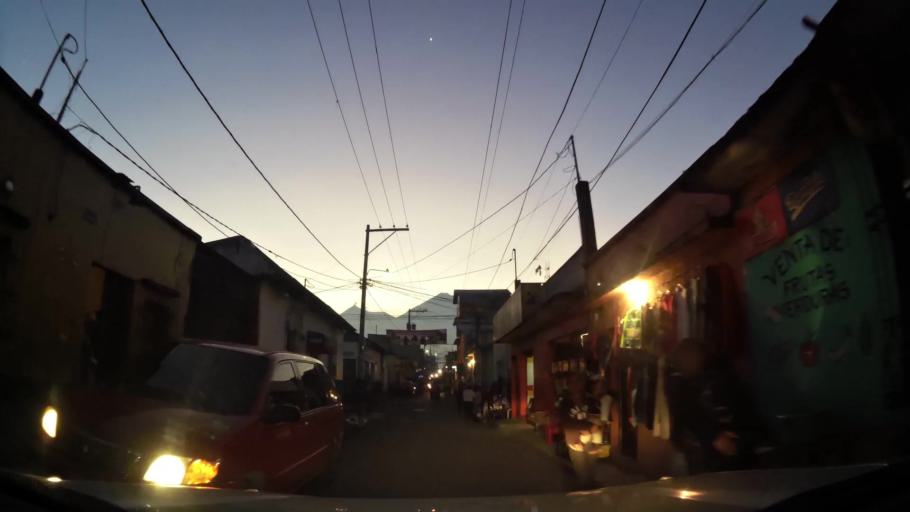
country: GT
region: Sacatepequez
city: Ciudad Vieja
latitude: 14.5237
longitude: -90.7645
